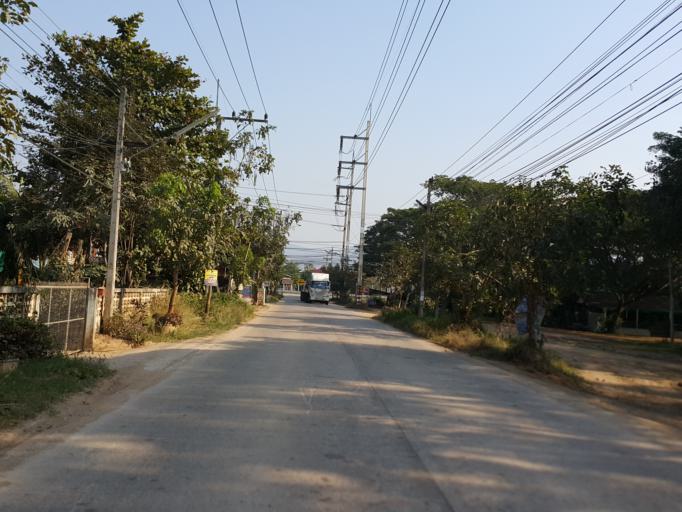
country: TH
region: Lampang
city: Lampang
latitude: 18.3415
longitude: 99.5412
